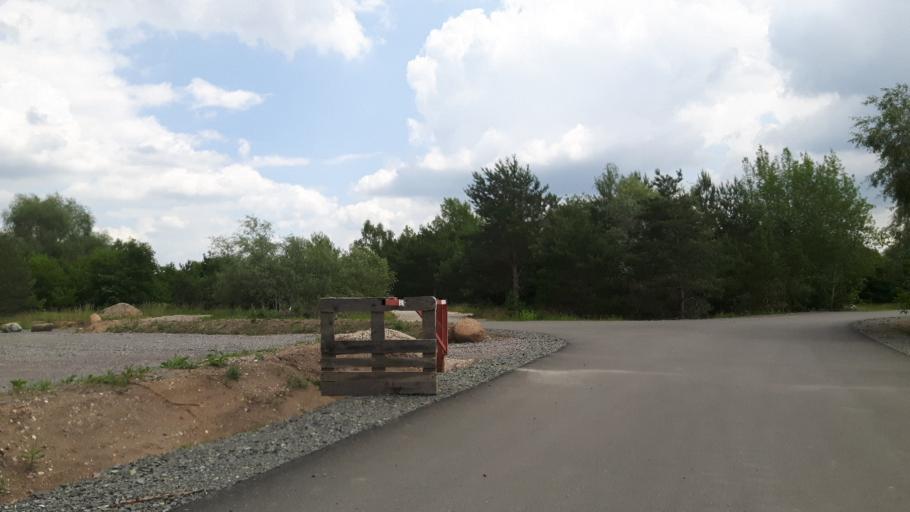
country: DE
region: Saxony-Anhalt
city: Grafenhainichen
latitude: 51.6950
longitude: 12.4562
